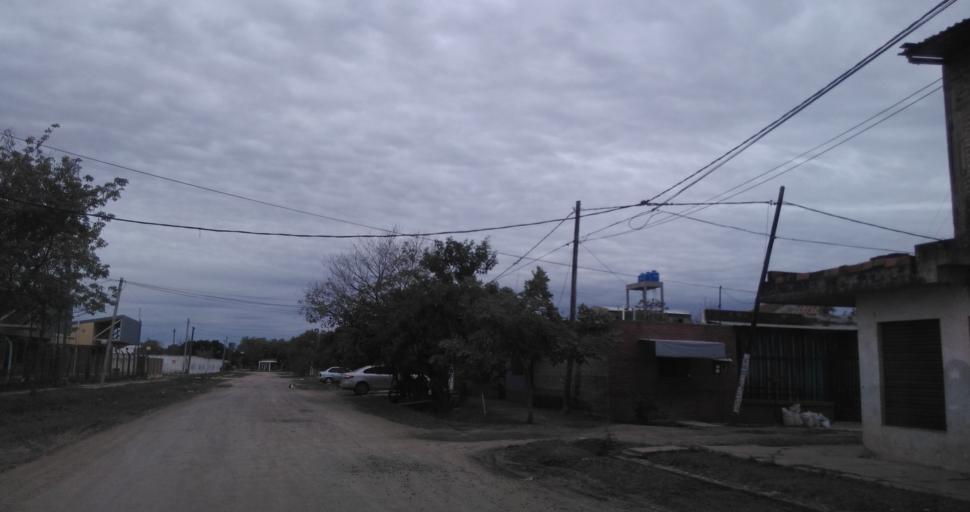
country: AR
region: Chaco
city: Resistencia
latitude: -27.4696
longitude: -58.9693
